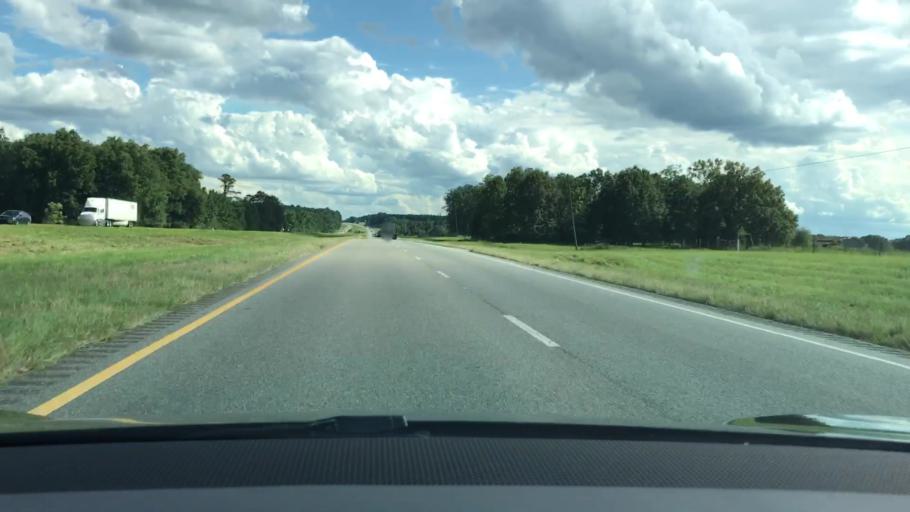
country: US
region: Alabama
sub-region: Montgomery County
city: Taylor
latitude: 32.0363
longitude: -86.0333
